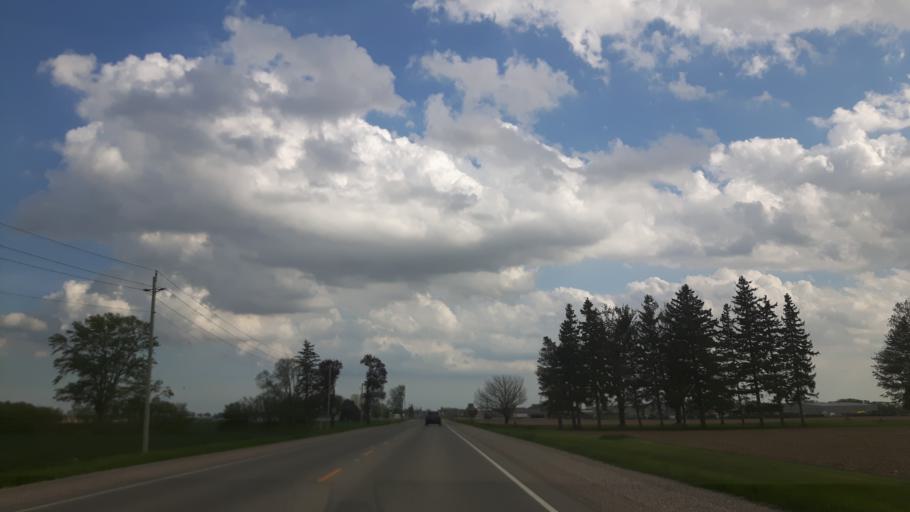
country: CA
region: Ontario
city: South Huron
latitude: 43.3726
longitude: -81.4859
